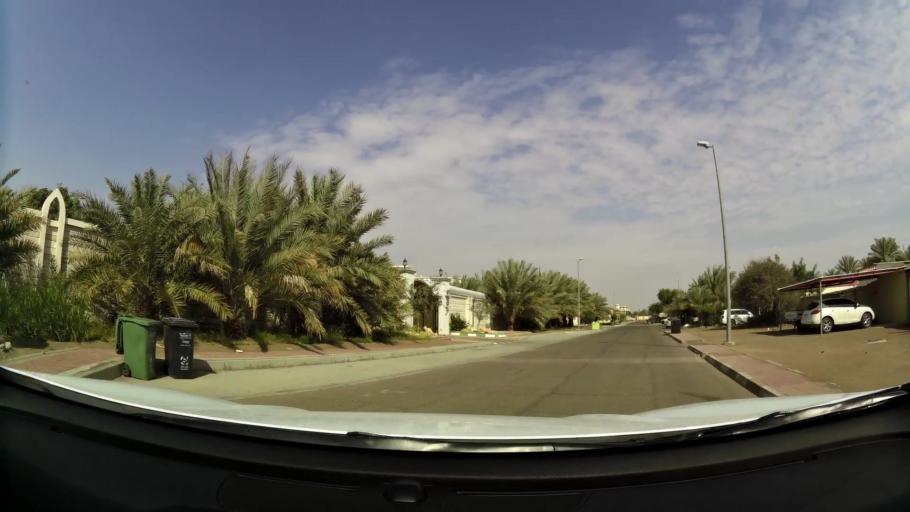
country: AE
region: Abu Dhabi
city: Al Ain
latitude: 24.0986
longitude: 55.9177
